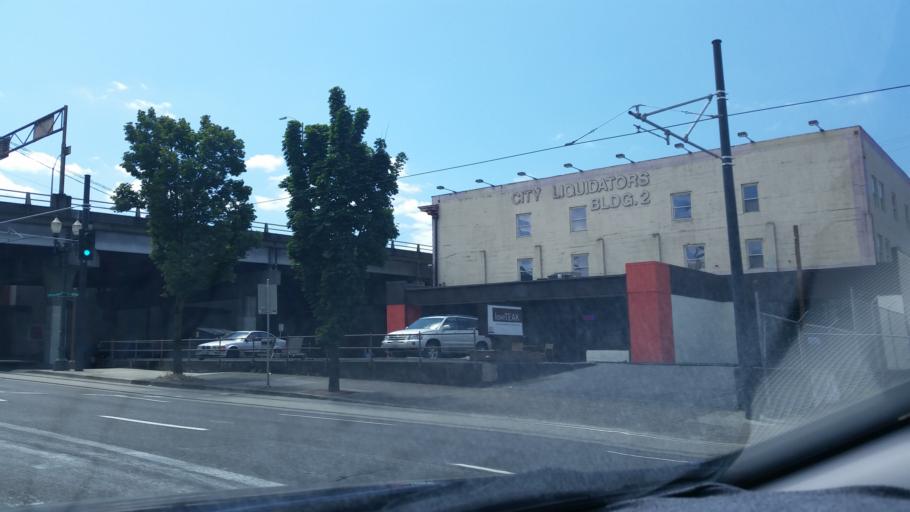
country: US
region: Oregon
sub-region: Multnomah County
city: Portland
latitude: 45.5170
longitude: -122.6617
